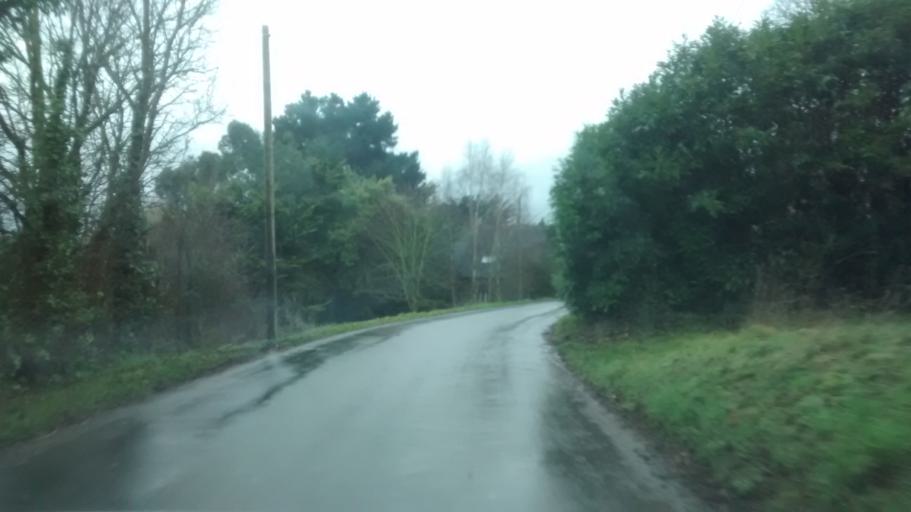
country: FR
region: Brittany
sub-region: Departement d'Ille-et-Vilaine
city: Saint-Meloir-des-Ondes
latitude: 48.6416
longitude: -1.8735
